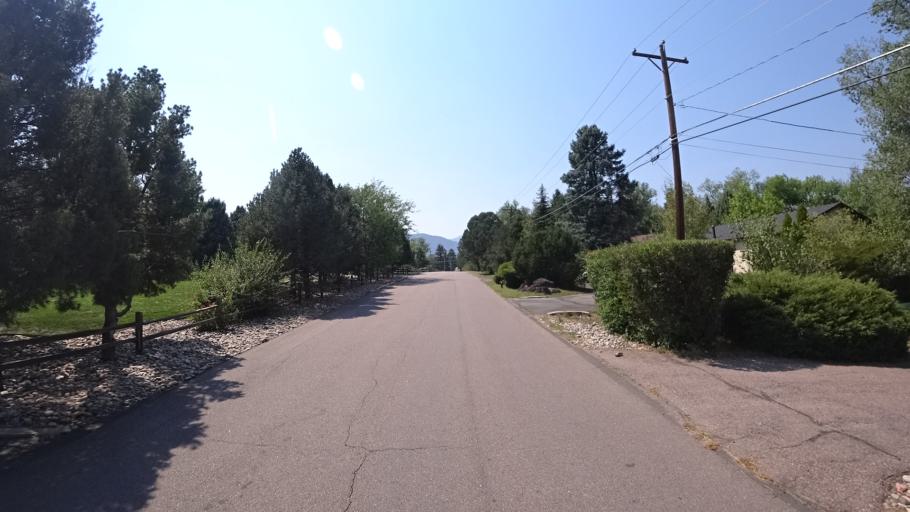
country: US
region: Colorado
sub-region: El Paso County
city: Colorado Springs
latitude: 38.7994
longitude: -104.8298
